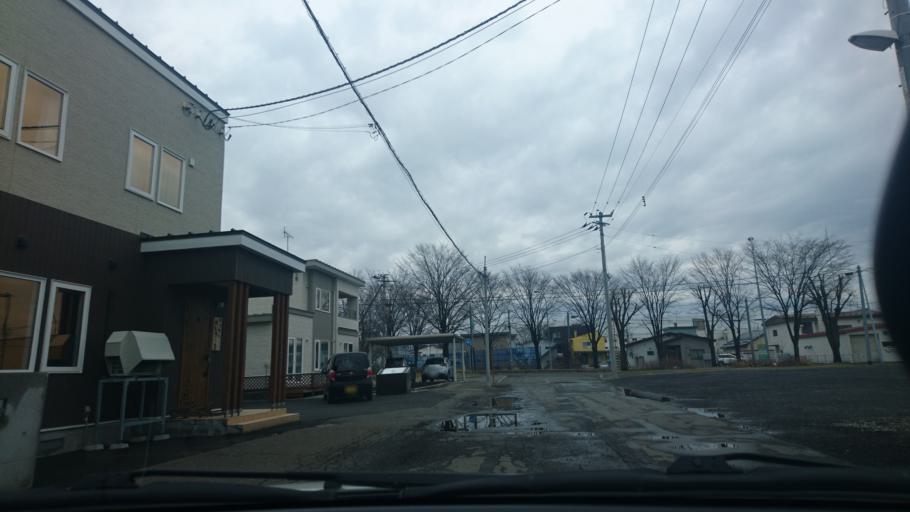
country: JP
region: Hokkaido
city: Obihiro
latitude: 42.9335
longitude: 143.1984
